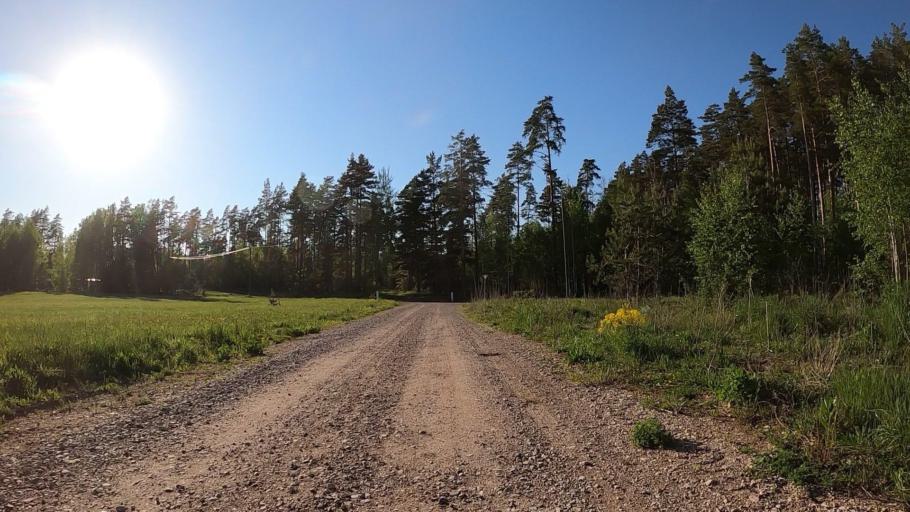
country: LV
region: Baldone
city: Baldone
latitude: 56.7745
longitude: 24.3253
